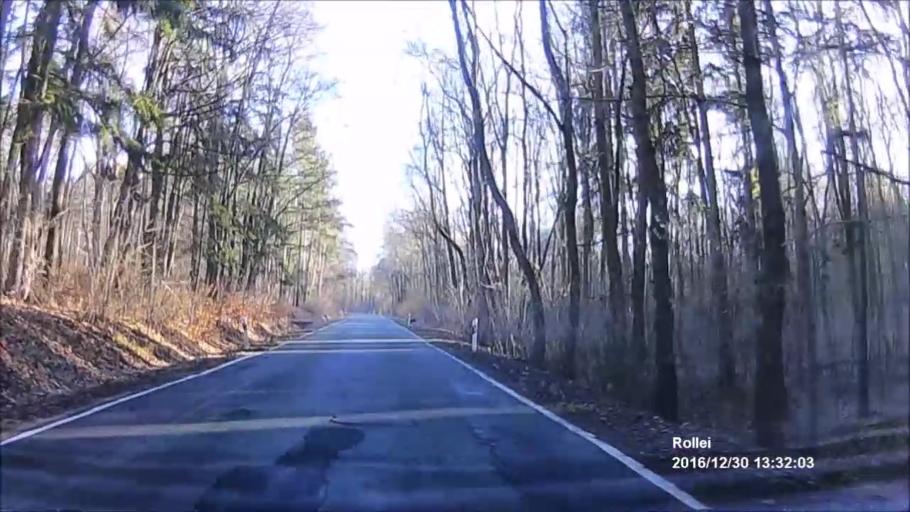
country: DE
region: Thuringia
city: Klettbach
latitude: 50.9313
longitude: 11.1042
